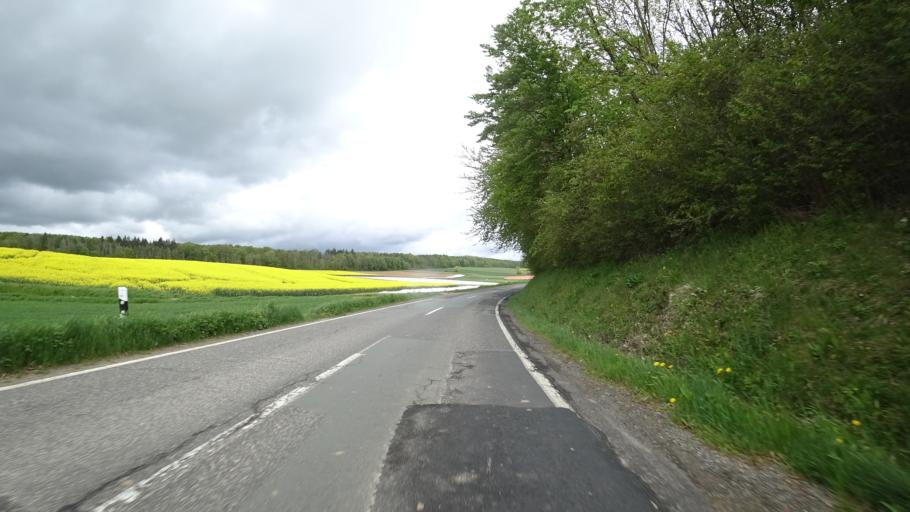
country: DE
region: Hesse
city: Grebenstein
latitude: 51.4419
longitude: 9.3602
